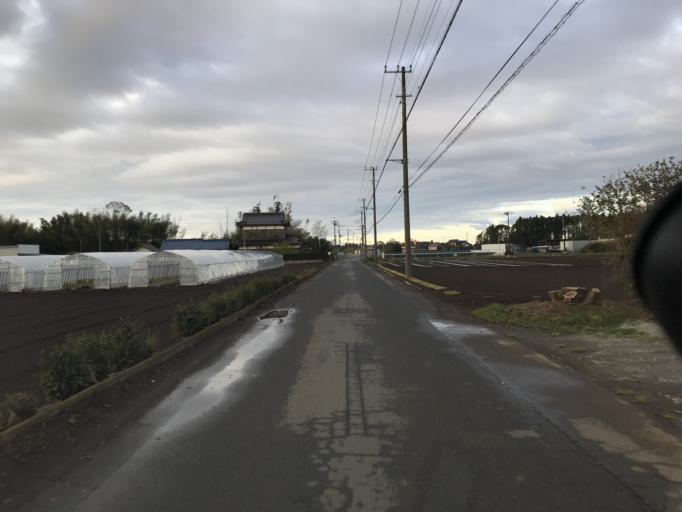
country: JP
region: Chiba
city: Sawara
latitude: 35.7880
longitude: 140.4468
